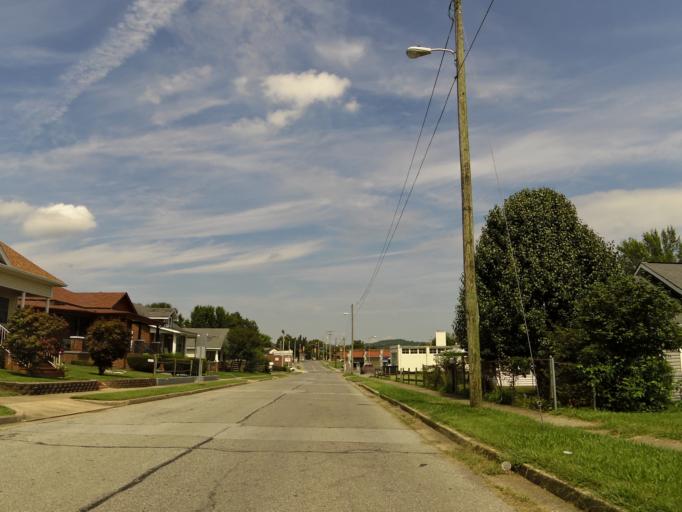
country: US
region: Tennessee
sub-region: Sullivan County
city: Kingsport
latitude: 36.5429
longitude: -82.5525
